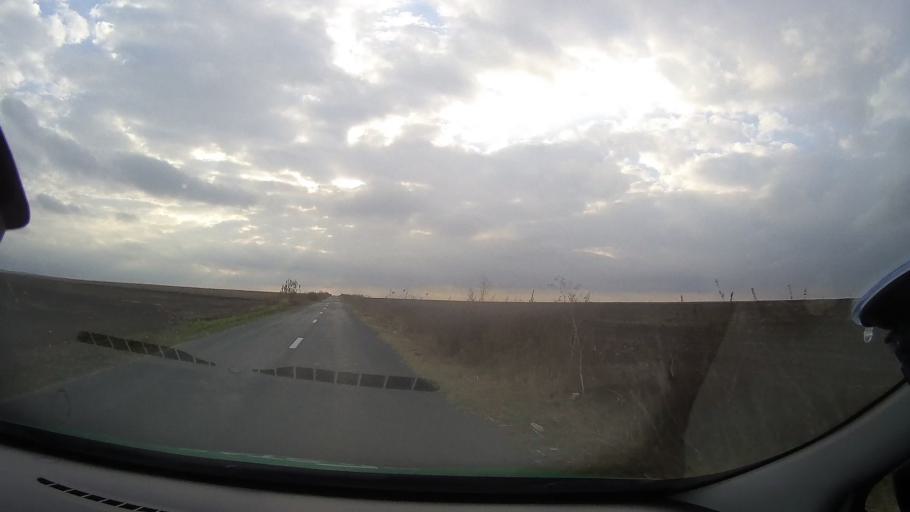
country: RO
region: Constanta
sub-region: Comuna Deleni
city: Pietreni
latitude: 44.1289
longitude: 28.1126
